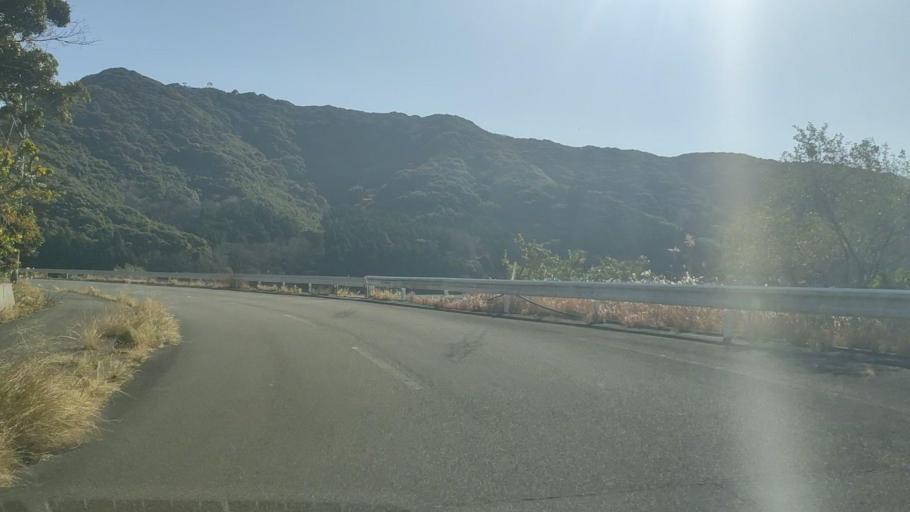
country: JP
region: Oita
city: Saiki
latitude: 32.7954
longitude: 131.8968
